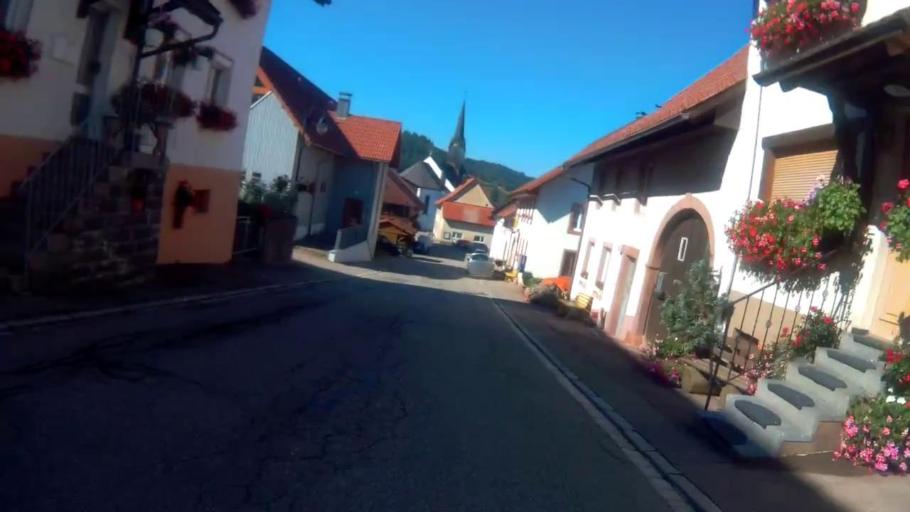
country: DE
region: Baden-Wuerttemberg
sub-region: Freiburg Region
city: Wembach
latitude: 47.7333
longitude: 7.9155
